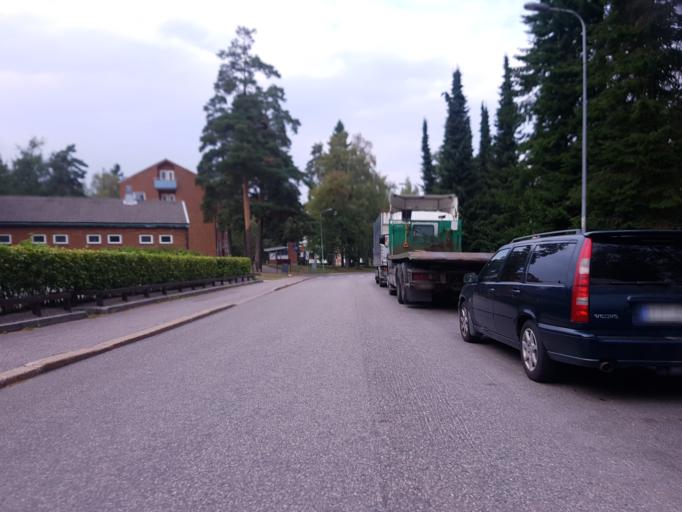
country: FI
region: Uusimaa
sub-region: Helsinki
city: Helsinki
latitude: 60.2283
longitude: 24.9504
